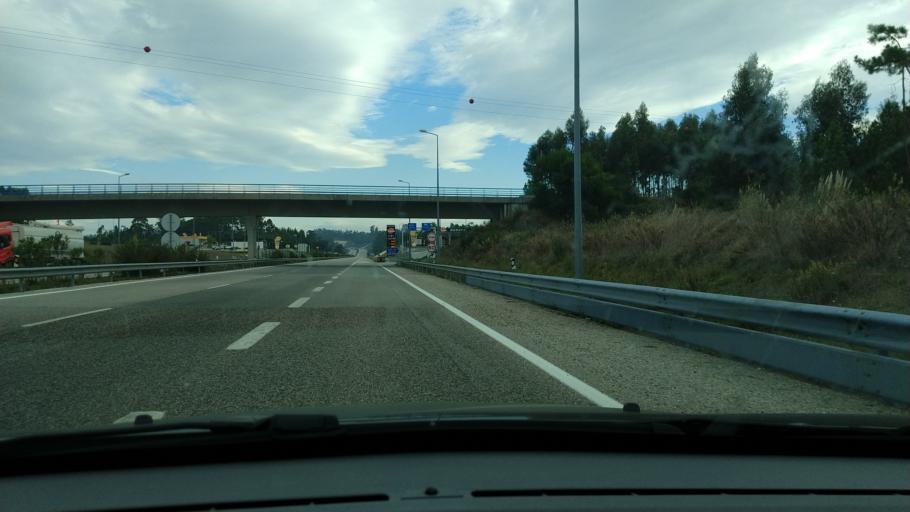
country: PT
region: Aveiro
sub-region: Vagos
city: Vagos
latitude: 40.5059
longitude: -8.6699
